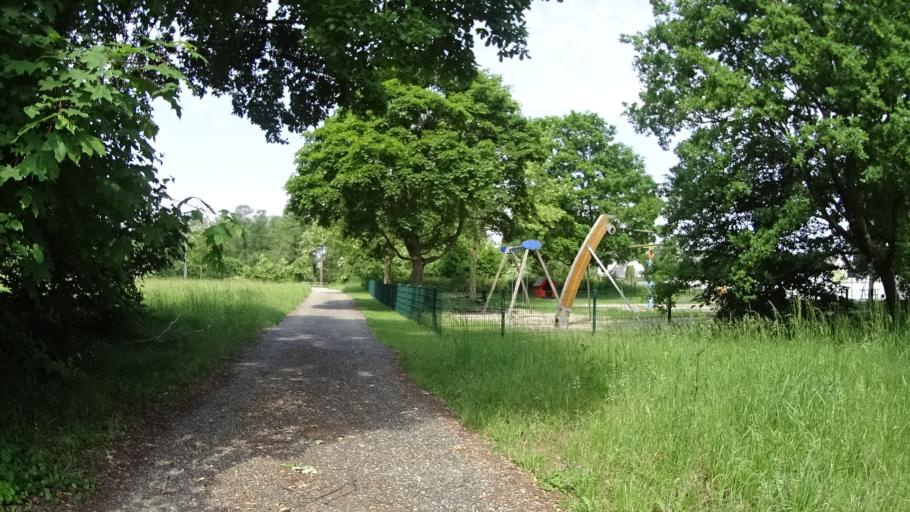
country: DE
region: Baden-Wuerttemberg
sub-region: Karlsruhe Region
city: Linkenheim-Hochstetten
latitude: 49.1122
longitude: 8.4132
